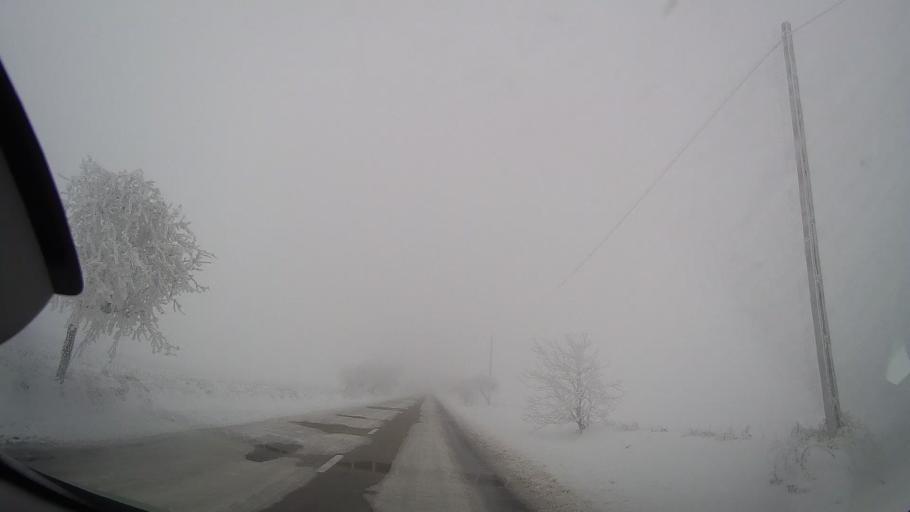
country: RO
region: Neamt
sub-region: Comuna Valea Ursului
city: Valea Ursului
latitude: 46.8057
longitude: 27.0707
